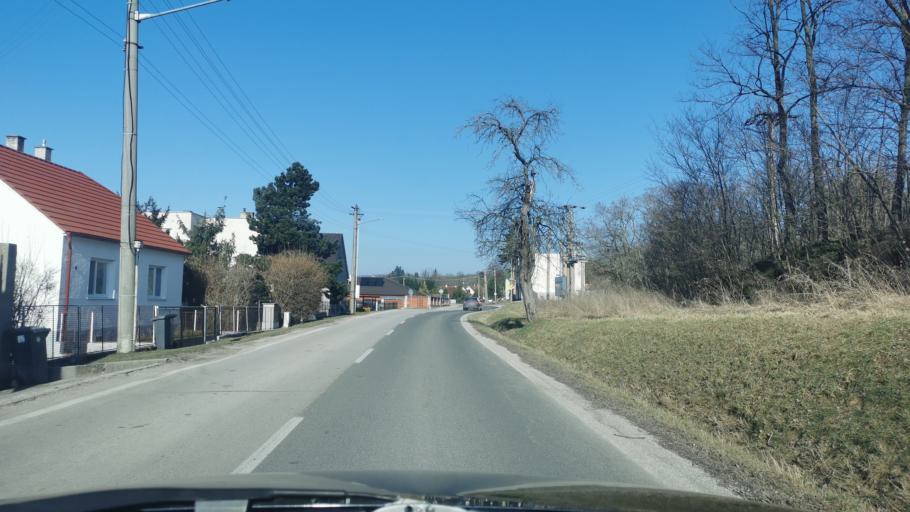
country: SK
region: Trnavsky
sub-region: Okres Senica
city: Senica
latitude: 48.6878
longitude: 17.3993
